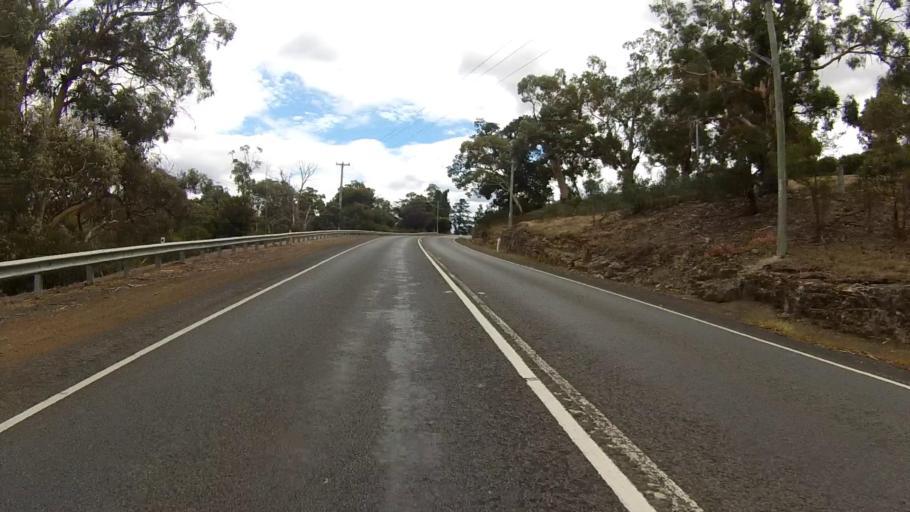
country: AU
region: Tasmania
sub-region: Brighton
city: Bridgewater
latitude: -42.6824
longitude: 147.2659
